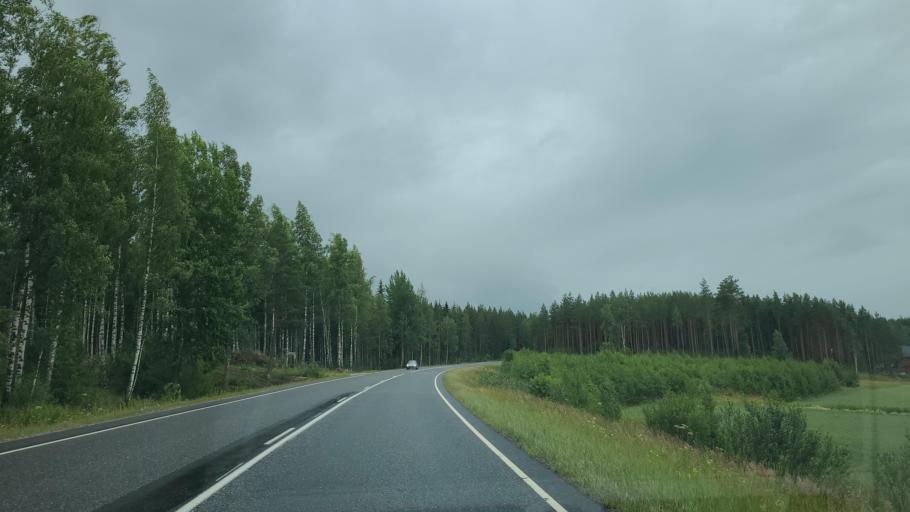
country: FI
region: Varsinais-Suomi
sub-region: Turku
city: Sauvo
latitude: 60.3275
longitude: 22.7141
